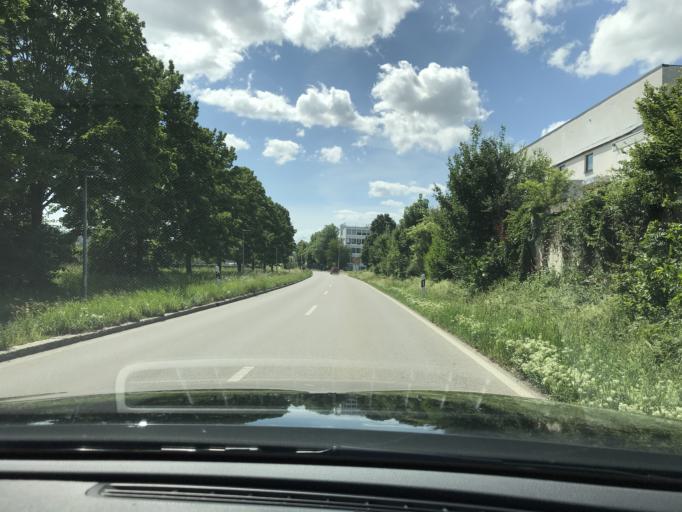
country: DE
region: Baden-Wuerttemberg
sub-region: Regierungsbezirk Stuttgart
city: Weinstadt-Endersbach
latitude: 48.8179
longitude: 9.3979
